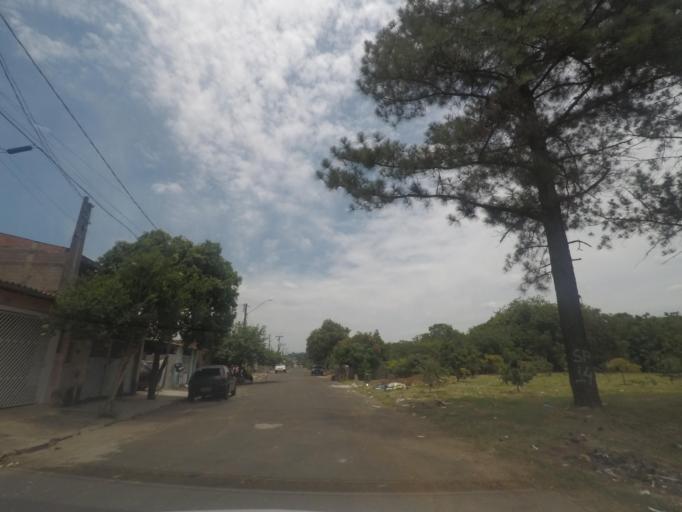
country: BR
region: Sao Paulo
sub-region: Nova Odessa
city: Nova Odessa
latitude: -22.7900
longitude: -47.2759
